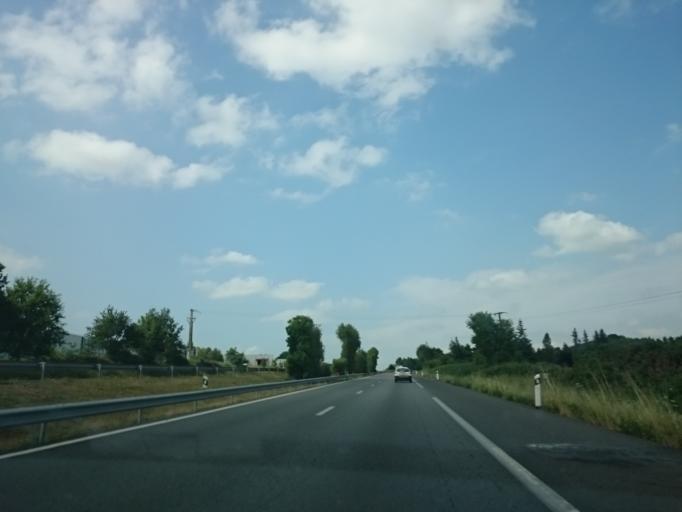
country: FR
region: Brittany
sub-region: Departement d'Ille-et-Vilaine
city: Crevin
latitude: 47.9243
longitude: -1.6767
